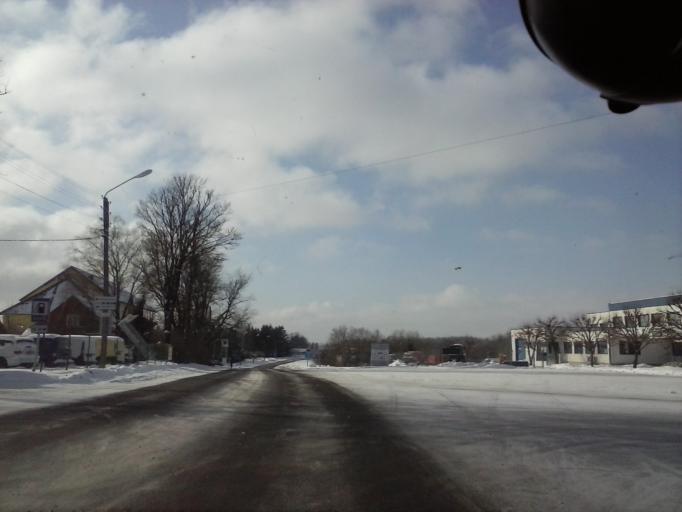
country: EE
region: Viljandimaa
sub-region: Viljandi linn
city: Viljandi
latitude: 58.3578
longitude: 25.5659
